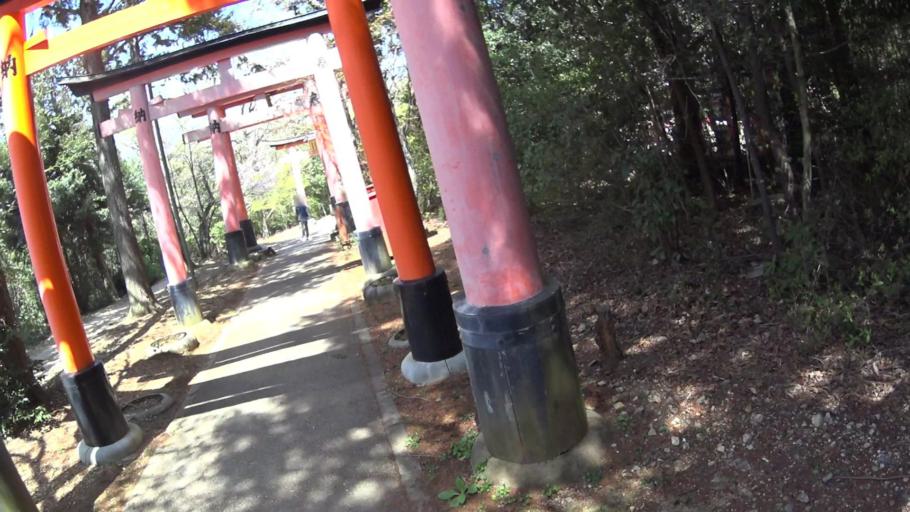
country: JP
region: Kyoto
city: Kyoto
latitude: 34.9707
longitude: 135.7803
